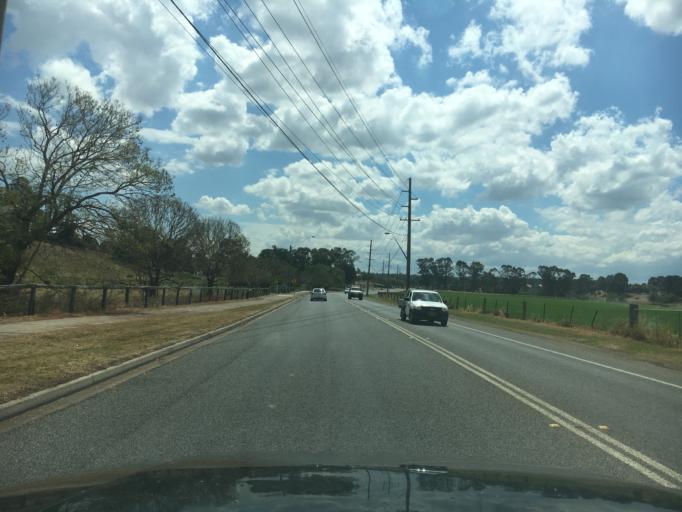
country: AU
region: New South Wales
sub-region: Singleton
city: Singleton
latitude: -32.5525
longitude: 151.1687
